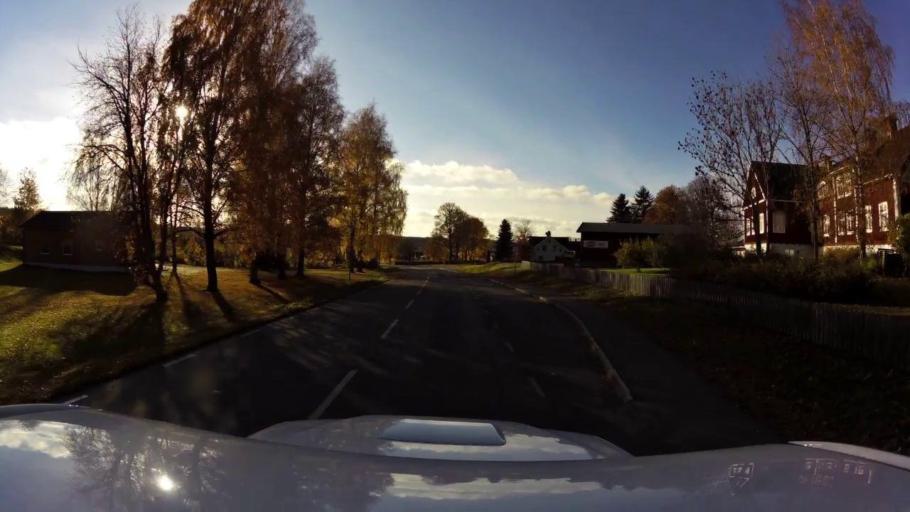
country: SE
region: OEstergoetland
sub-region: Linkopings Kommun
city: Vikingstad
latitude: 58.2882
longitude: 15.4483
